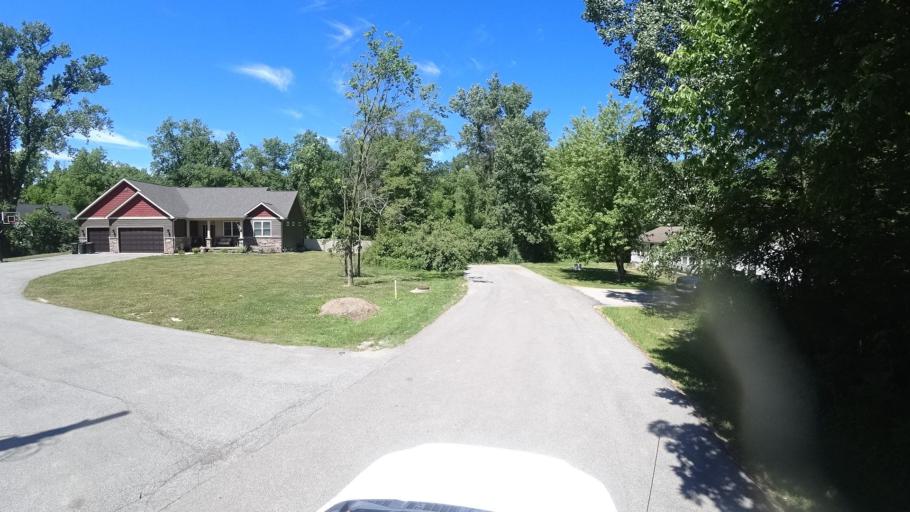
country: US
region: Indiana
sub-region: Porter County
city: Porter
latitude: 41.6387
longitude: -87.0584
